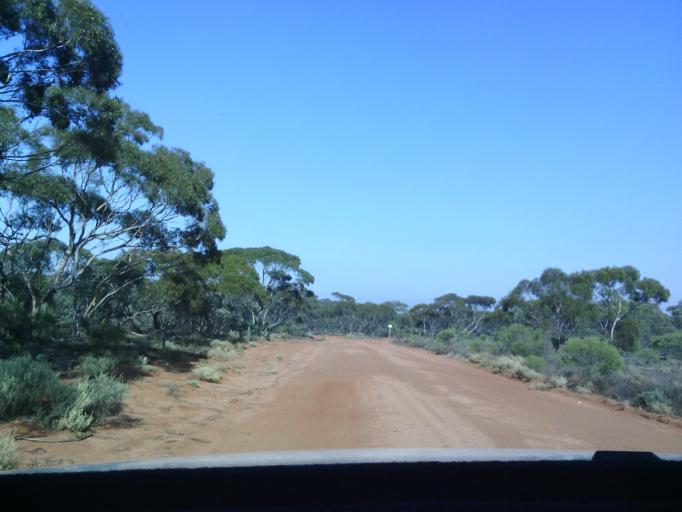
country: AU
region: South Australia
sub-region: Berri and Barmera
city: Monash
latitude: -34.2250
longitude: 140.5817
